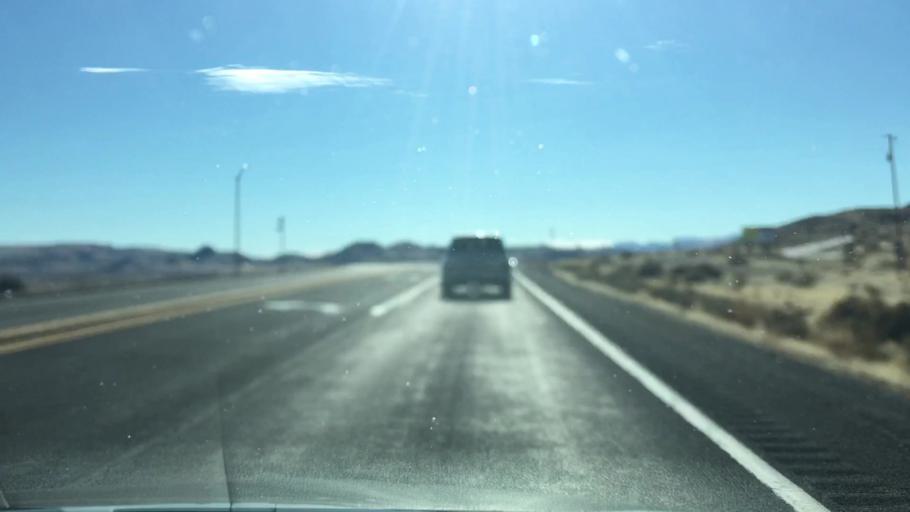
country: US
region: Nevada
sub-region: Lyon County
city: Silver Springs
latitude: 39.3329
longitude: -119.2414
